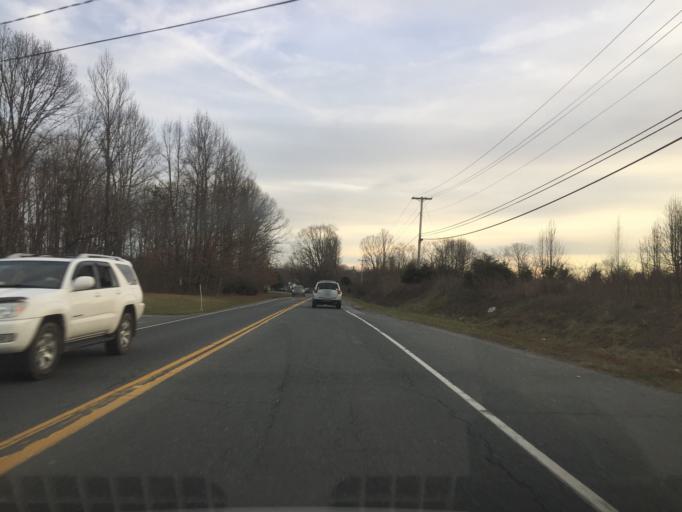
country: US
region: Virginia
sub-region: Bedford County
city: Forest
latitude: 37.3481
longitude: -79.2831
